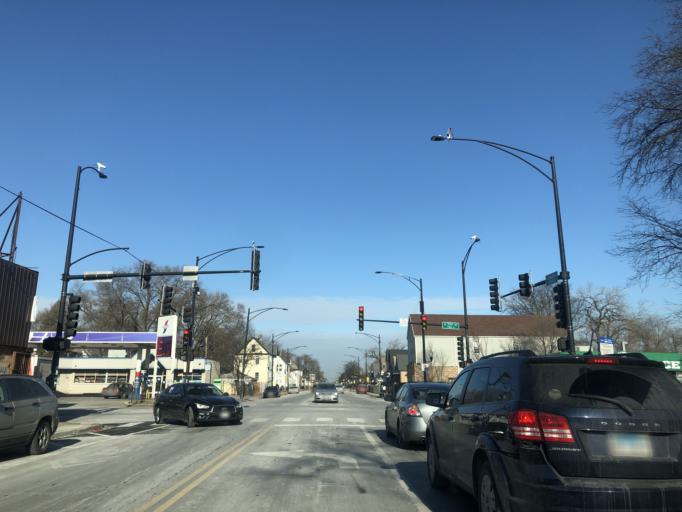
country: US
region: Illinois
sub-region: Cook County
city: Evergreen Park
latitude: 41.7645
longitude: -87.6735
